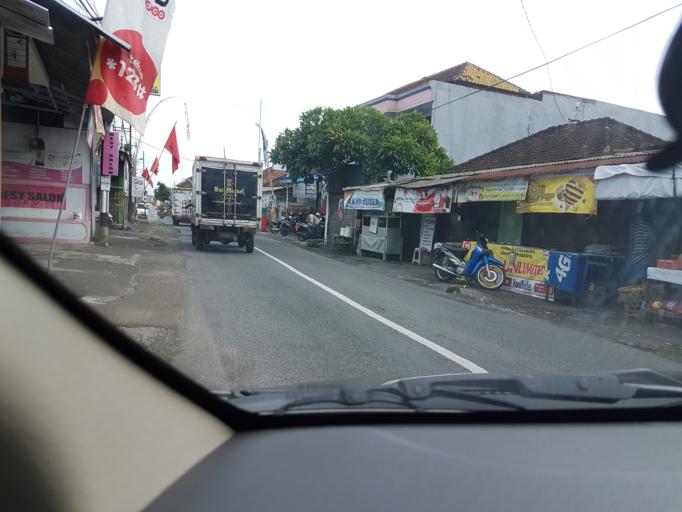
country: ID
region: Bali
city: Denpasar
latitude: -8.6665
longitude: 115.1921
